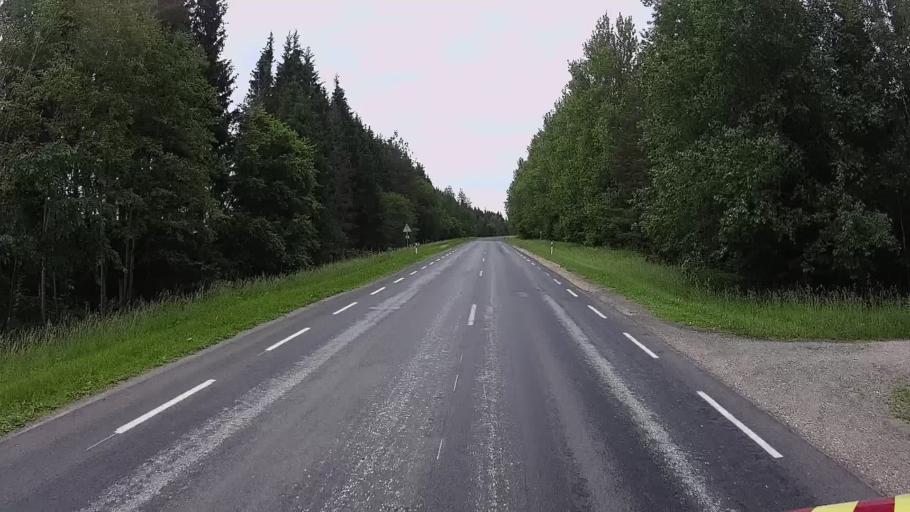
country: EE
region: Viljandimaa
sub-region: Karksi vald
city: Karksi-Nuia
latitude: 58.2073
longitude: 25.6210
